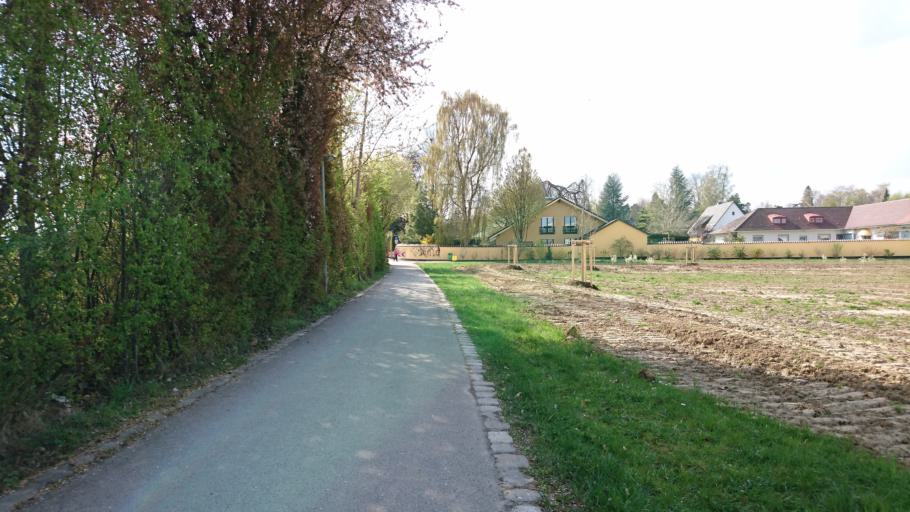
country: DE
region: Bavaria
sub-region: Swabia
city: Stadtbergen
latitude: 48.3835
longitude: 10.8309
